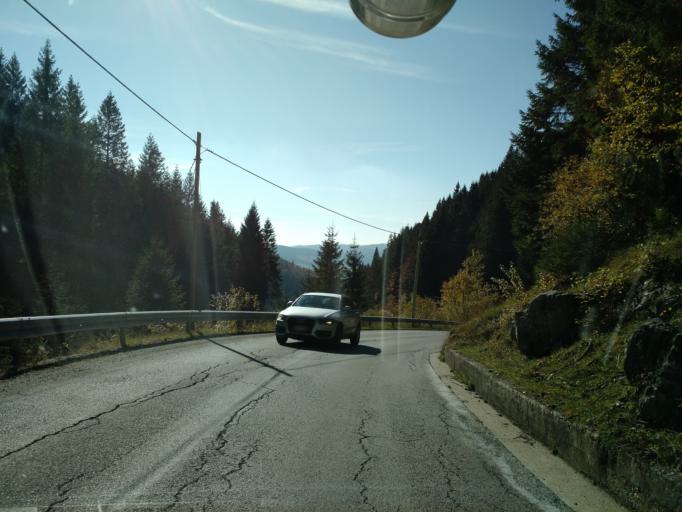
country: IT
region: Veneto
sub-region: Provincia di Vicenza
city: Gallio
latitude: 45.9123
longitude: 11.5679
